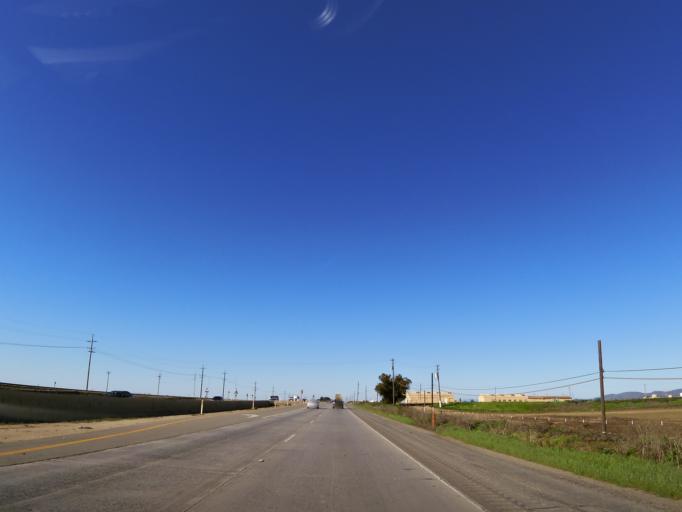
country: US
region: California
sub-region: Monterey County
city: Chualar
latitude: 36.5945
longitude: -121.5443
